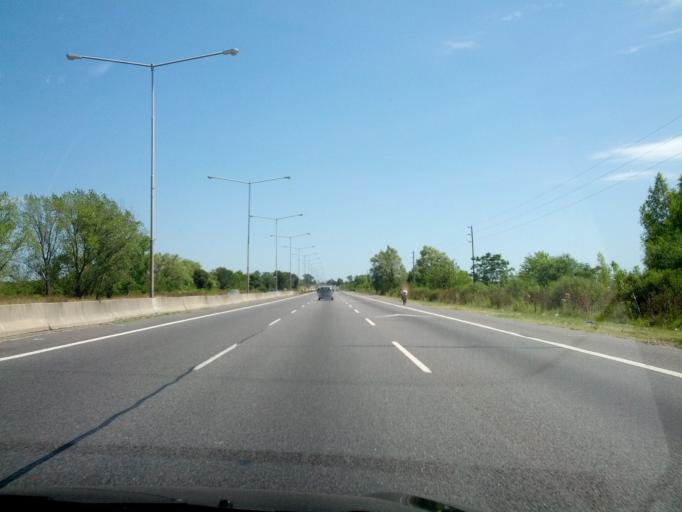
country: AR
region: Buenos Aires
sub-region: Partido de Campana
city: Campana
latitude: -34.2627
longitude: -58.9017
